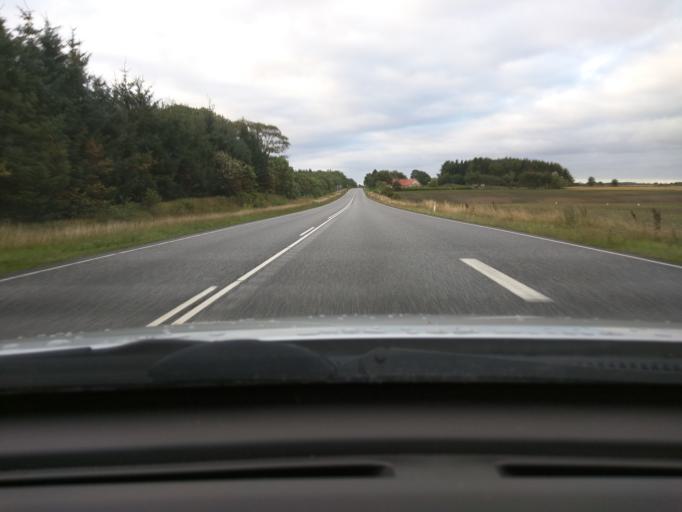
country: DK
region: Central Jutland
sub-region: Silkeborg Kommune
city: Kjellerup
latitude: 56.2962
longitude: 9.3220
